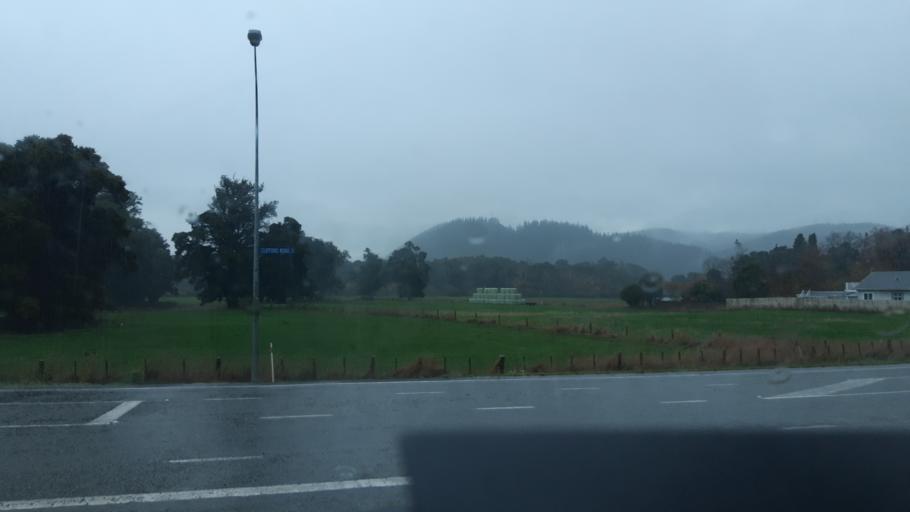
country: NZ
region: Tasman
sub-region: Tasman District
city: Wakefield
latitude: -41.4087
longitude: 173.0376
